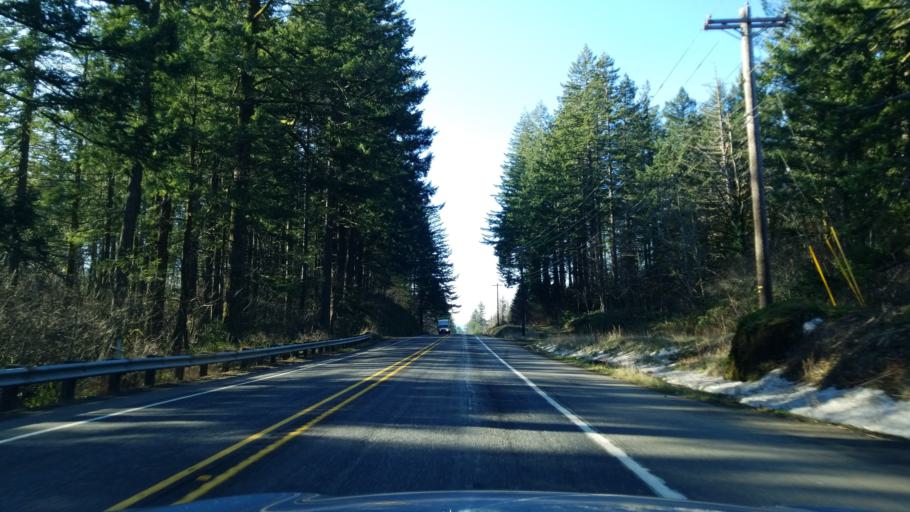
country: US
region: Washington
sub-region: Clark County
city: Washougal
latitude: 45.5970
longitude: -122.1288
